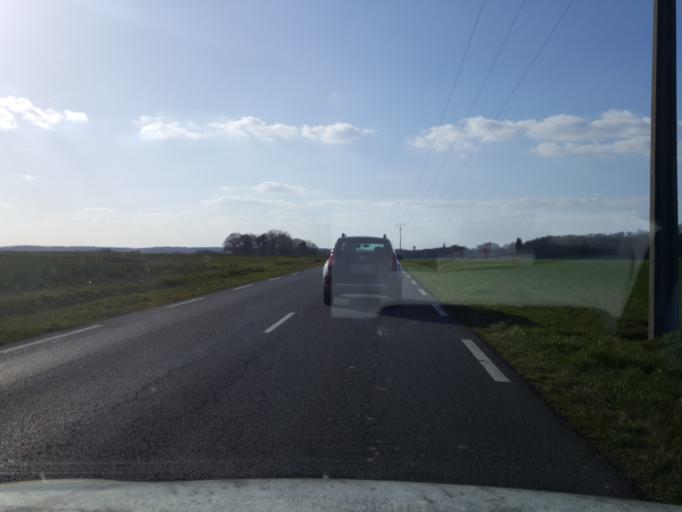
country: FR
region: Centre
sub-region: Departement d'Eure-et-Loir
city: Droue-sur-Drouette
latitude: 48.6501
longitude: 1.7073
